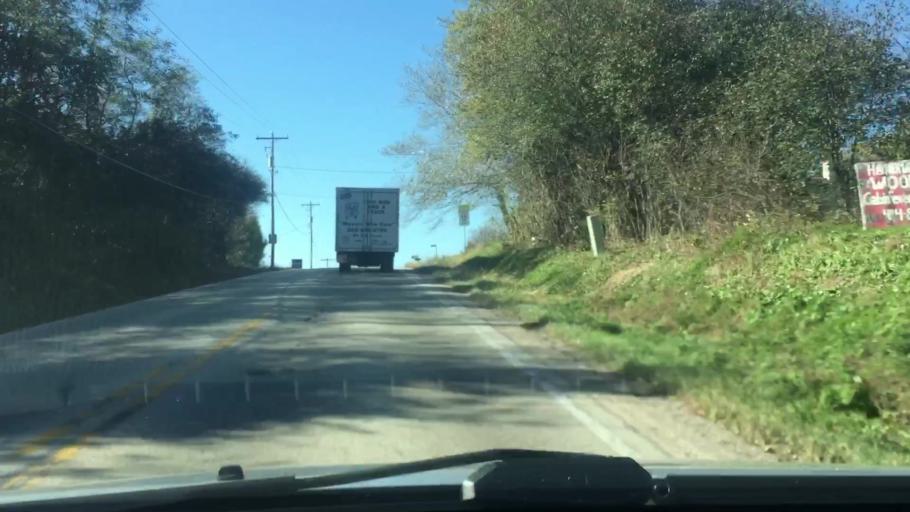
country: US
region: Wisconsin
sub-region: Waukesha County
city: Wales
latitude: 42.9881
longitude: -88.3354
